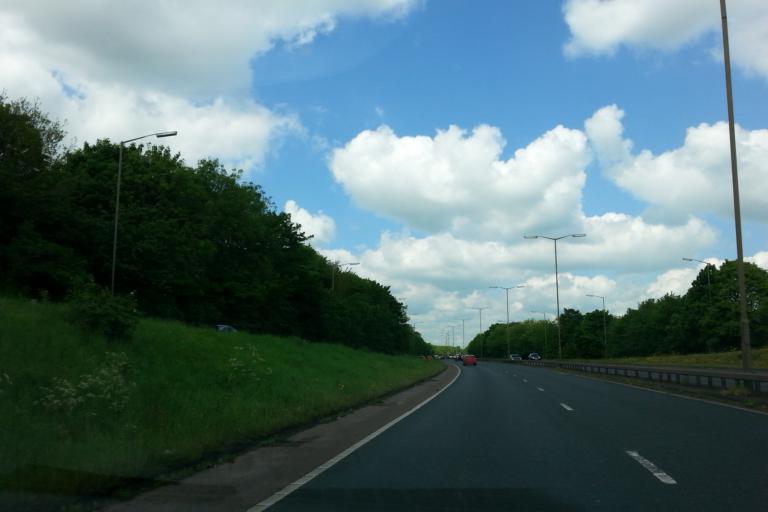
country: GB
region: England
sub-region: Peterborough
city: Peterborough
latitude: 52.5525
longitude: -0.2685
